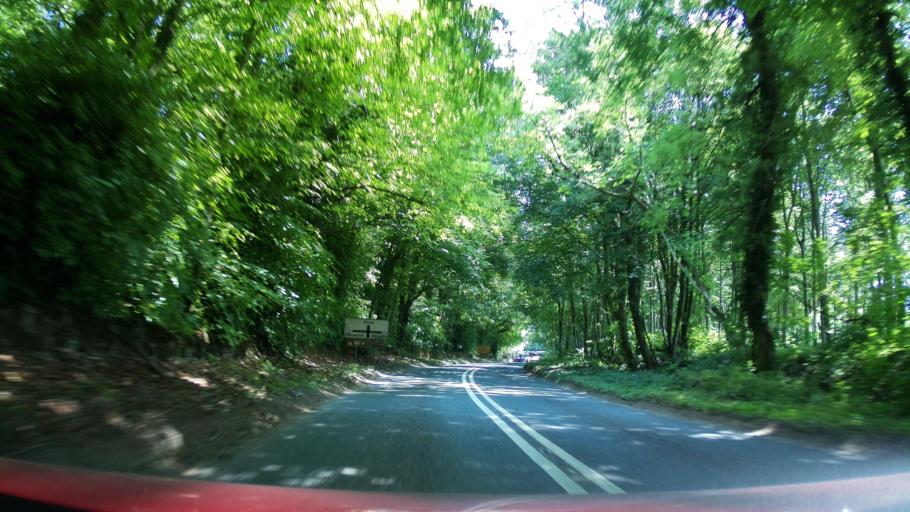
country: GB
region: England
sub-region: Gloucestershire
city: Westfield
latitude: 51.9570
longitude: -1.8485
